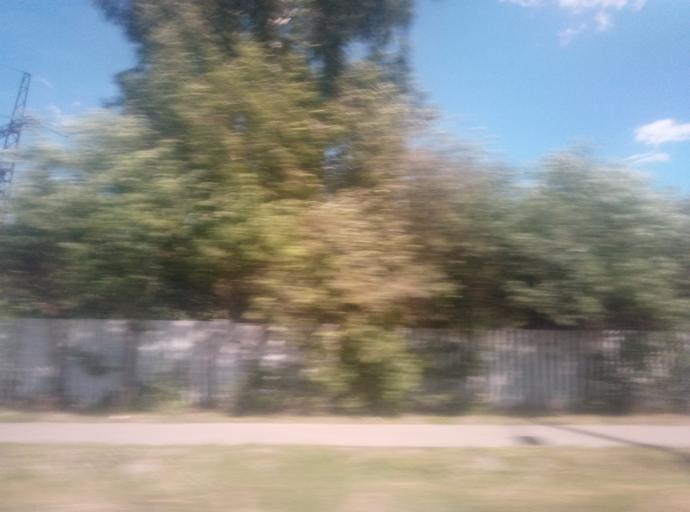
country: RU
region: Tula
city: Kireyevsk
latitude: 54.0163
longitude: 37.9166
